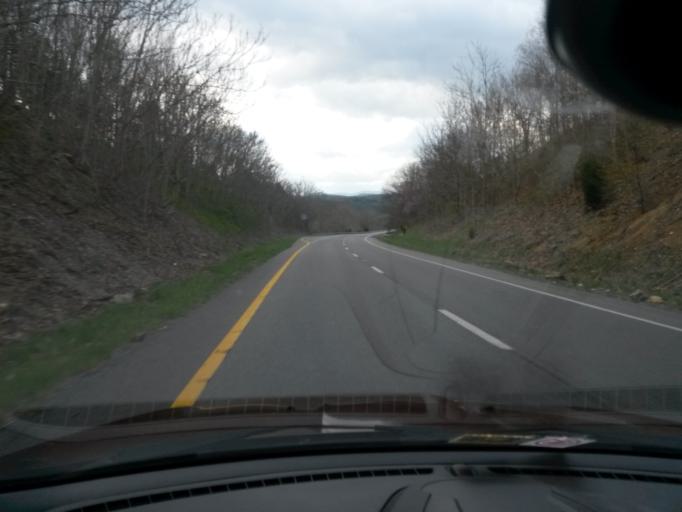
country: US
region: Virginia
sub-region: Botetourt County
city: Fincastle
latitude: 37.5866
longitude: -79.8338
